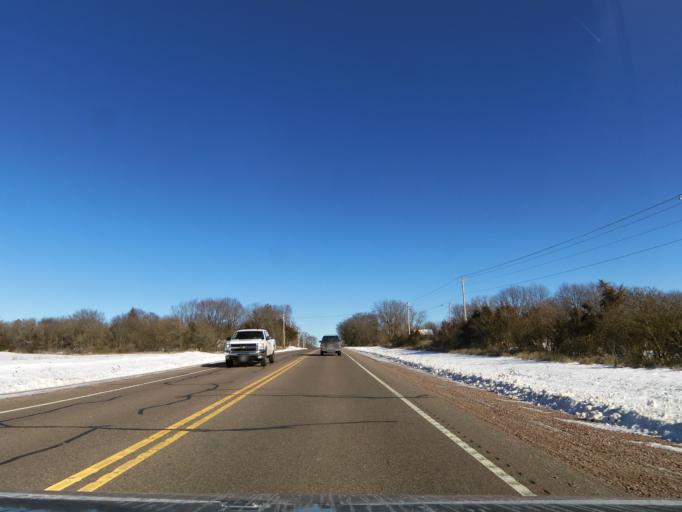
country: US
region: Wisconsin
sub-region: Sauk County
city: Baraboo
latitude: 43.4757
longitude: -89.6528
